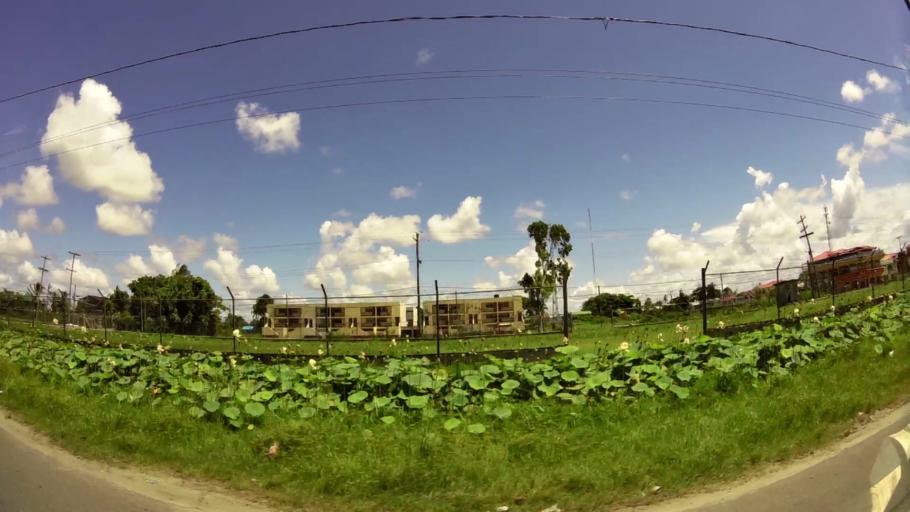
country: GY
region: Demerara-Mahaica
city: Georgetown
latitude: 6.7883
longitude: -58.1468
